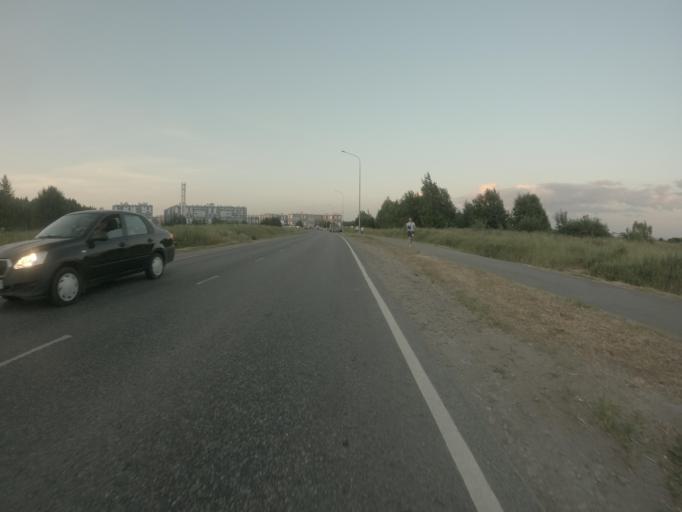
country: RU
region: Leningrad
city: Yanino Vtoroye
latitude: 59.9559
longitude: 30.5863
